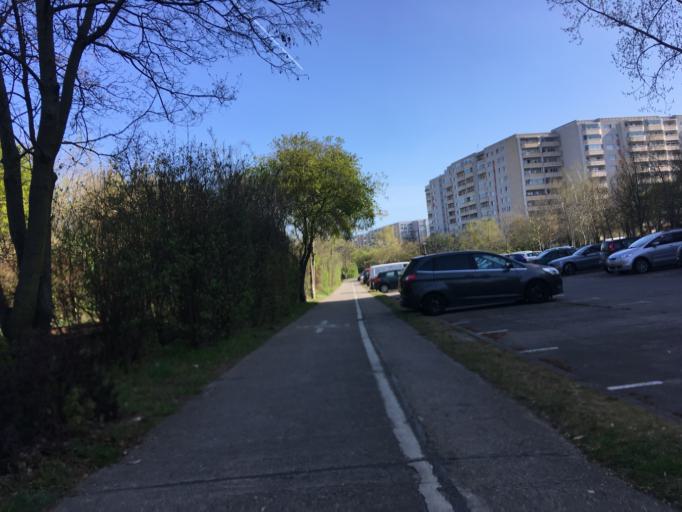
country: DE
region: Berlin
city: Marzahn
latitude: 52.5493
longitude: 13.5601
